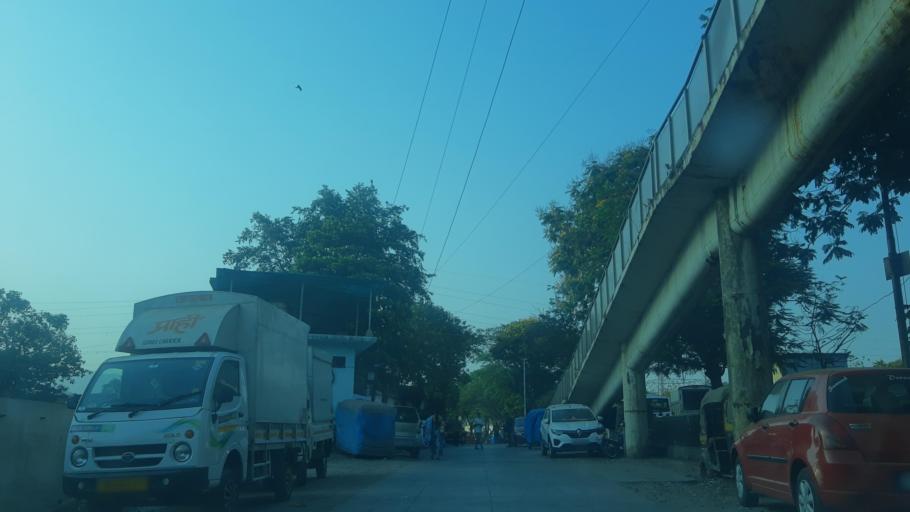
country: IN
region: Maharashtra
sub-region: Thane
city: Thane
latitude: 19.1771
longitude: 72.9677
